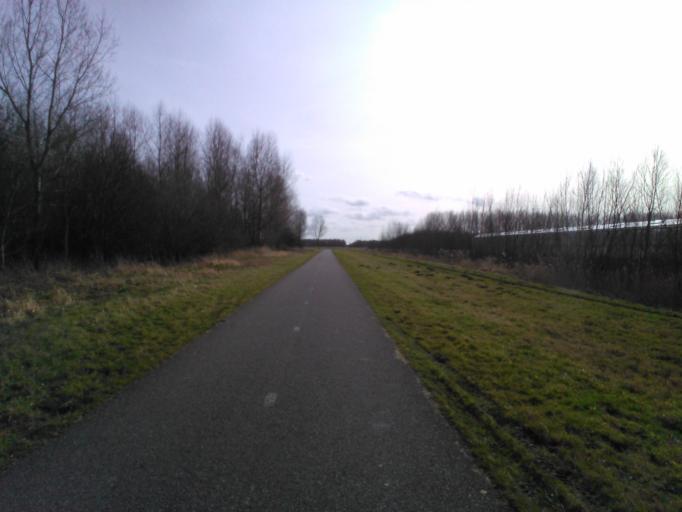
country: NL
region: South Holland
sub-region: Gemeente Pijnacker-Nootdorp
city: Pijnacker
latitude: 52.0440
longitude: 4.4372
